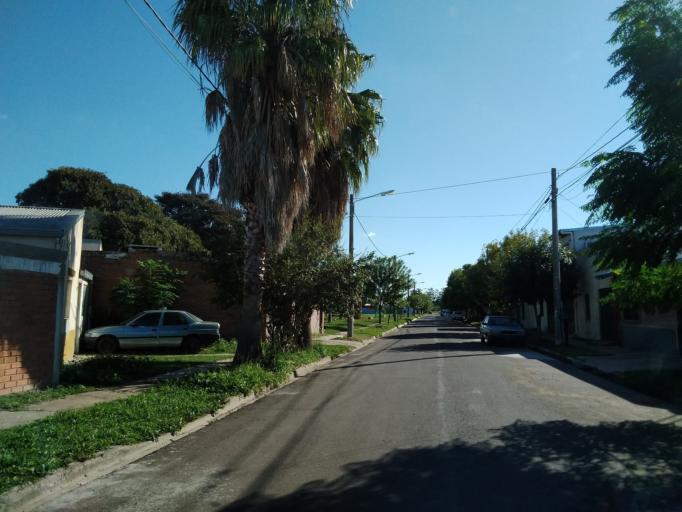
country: AR
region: Corrientes
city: Corrientes
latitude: -27.4581
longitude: -58.7667
